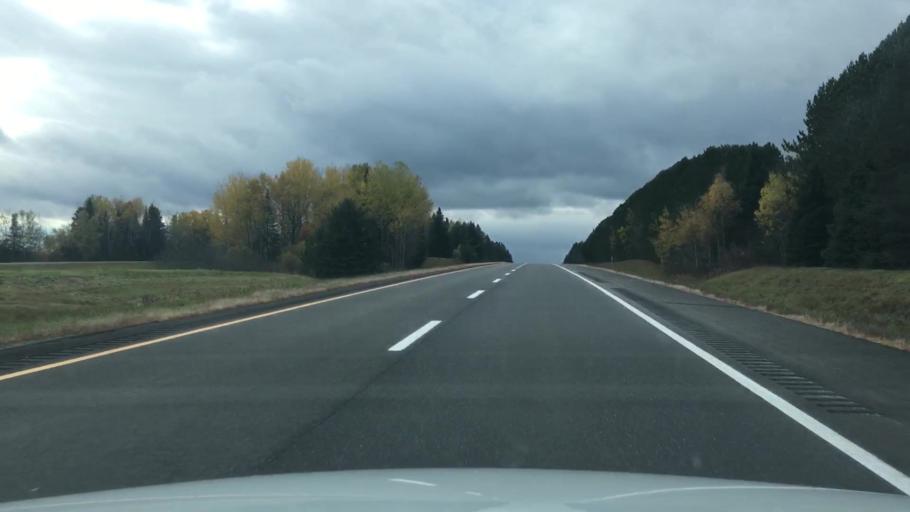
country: US
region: Maine
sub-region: Penobscot County
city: Patten
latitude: 46.0985
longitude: -68.1865
